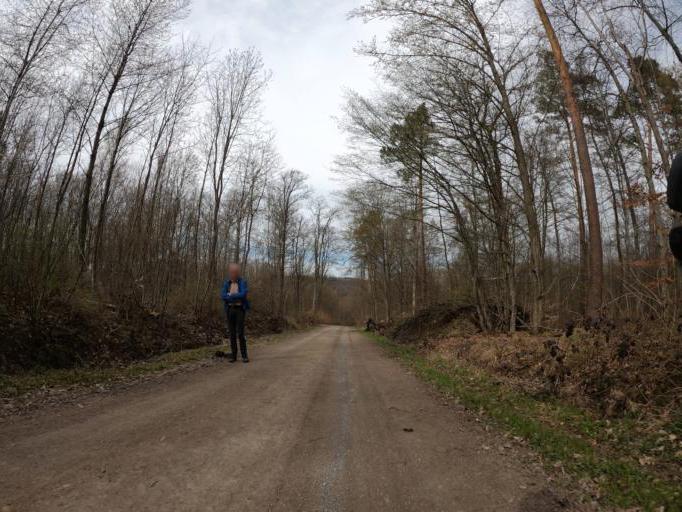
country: DE
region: Baden-Wuerttemberg
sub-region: Regierungsbezirk Stuttgart
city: Waldenbuch
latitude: 48.6290
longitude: 9.1662
